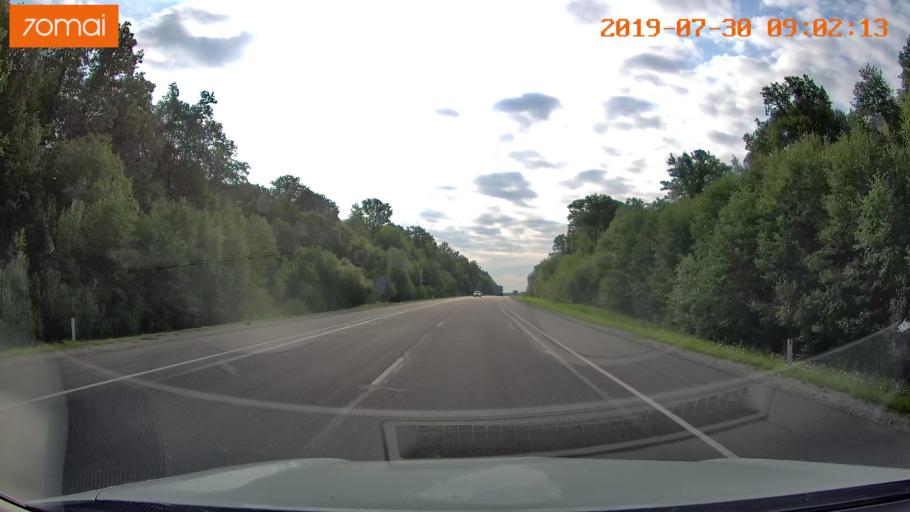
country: RU
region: Kaliningrad
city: Gusev
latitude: 54.6170
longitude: 22.2266
